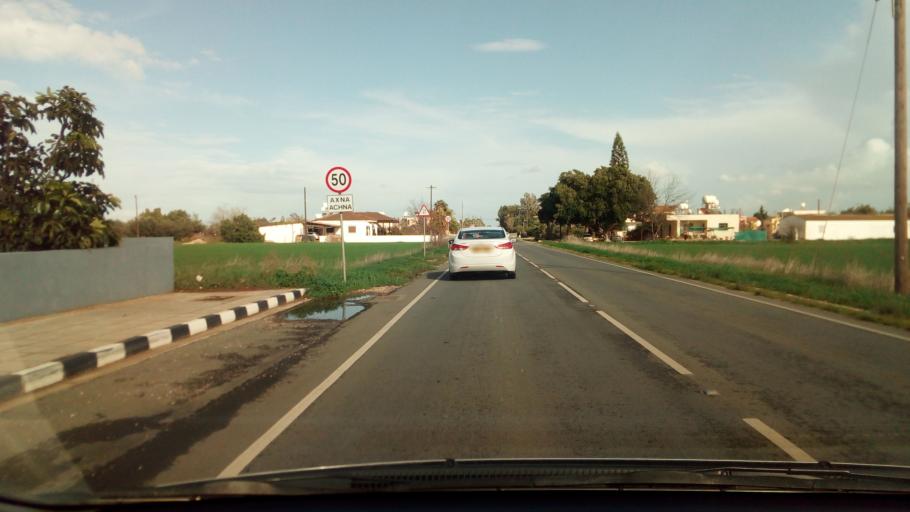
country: CY
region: Larnaka
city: Xylotymbou
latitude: 35.0327
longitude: 33.7583
